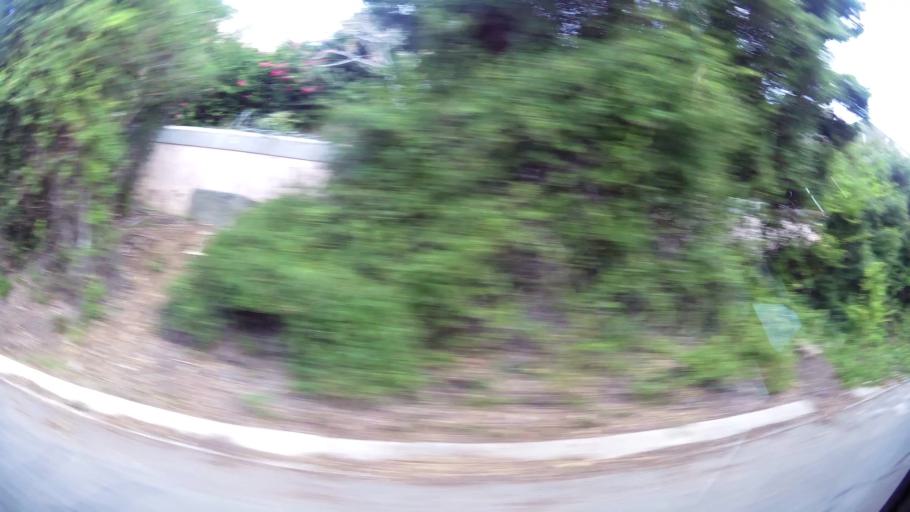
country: ZA
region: Western Cape
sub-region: Eden District Municipality
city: Plettenberg Bay
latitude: -34.0484
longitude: 23.3696
